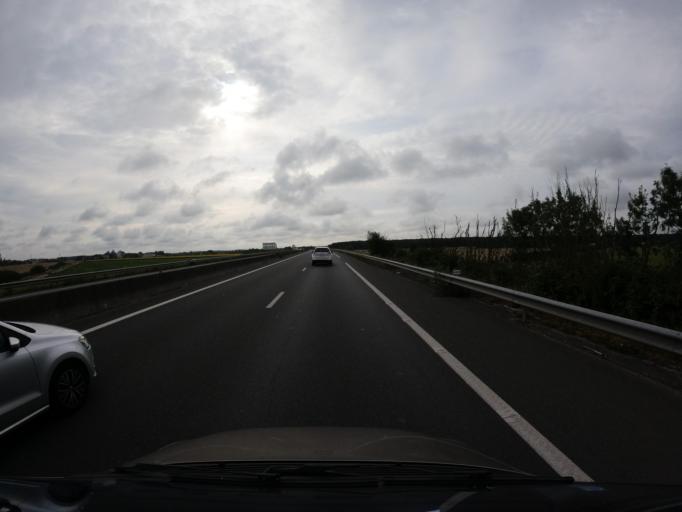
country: FR
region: Centre
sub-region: Departement d'Indre-et-Loire
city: Villandry
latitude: 47.3039
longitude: 0.5238
